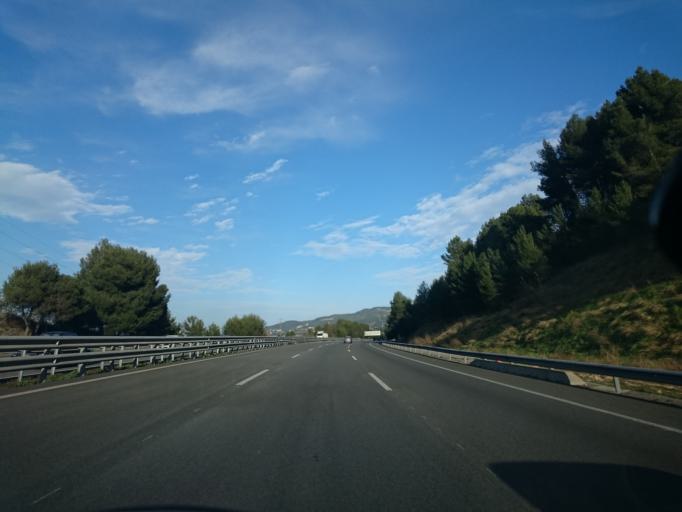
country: ES
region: Catalonia
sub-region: Provincia de Barcelona
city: Sant Sadurni d'Anoia
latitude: 41.4193
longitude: 1.7978
